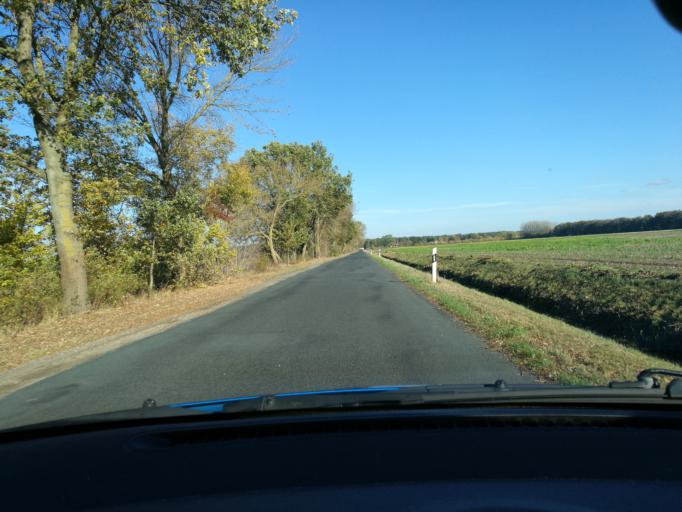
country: DE
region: Mecklenburg-Vorpommern
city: Neu Kaliss
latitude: 53.1511
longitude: 11.3082
